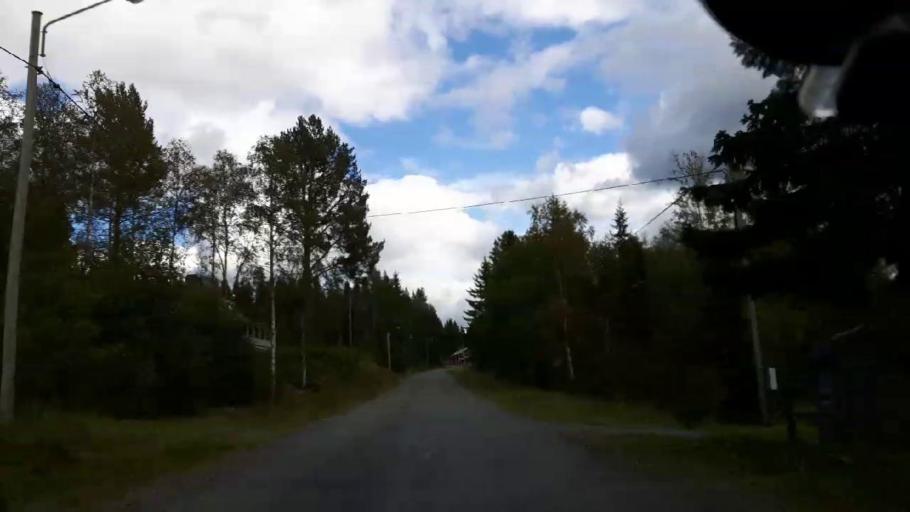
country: SE
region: Jaemtland
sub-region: Stroemsunds Kommun
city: Stroemsund
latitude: 63.4206
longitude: 15.8351
